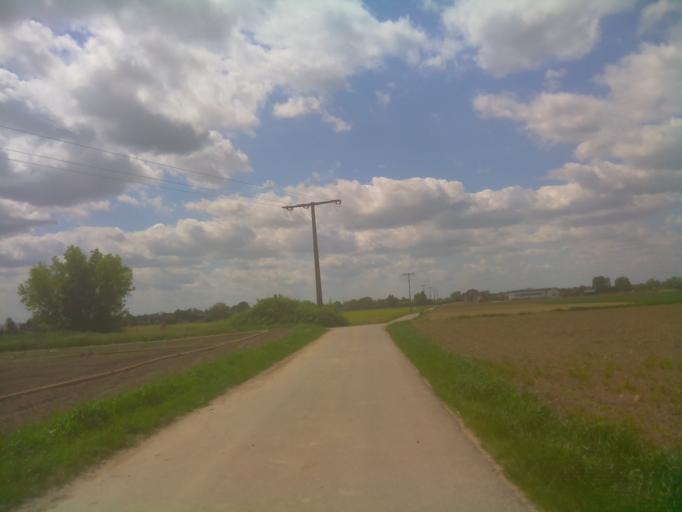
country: DE
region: Rheinland-Pfalz
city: Otterstadt
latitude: 49.3833
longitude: 8.4527
